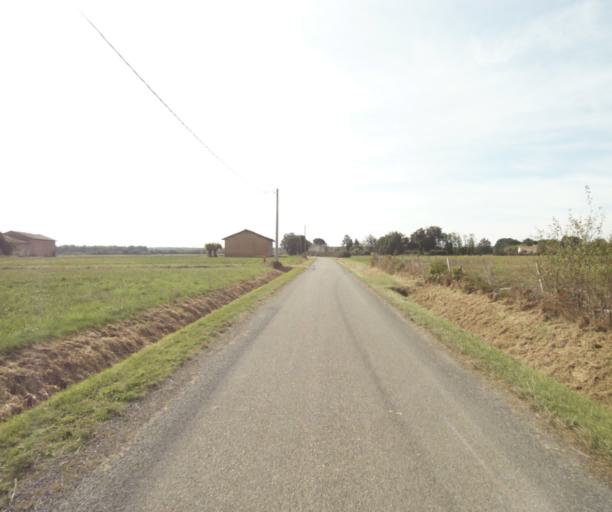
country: FR
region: Midi-Pyrenees
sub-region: Departement du Tarn-et-Garonne
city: Campsas
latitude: 43.8849
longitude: 1.3527
